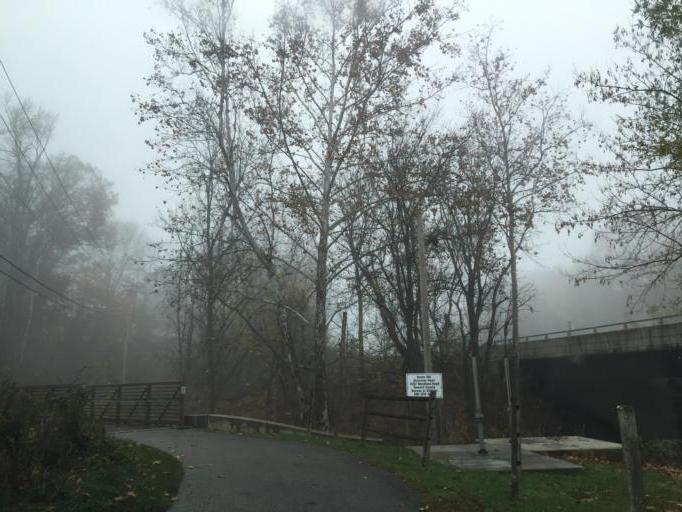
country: US
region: Maryland
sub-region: Howard County
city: Columbia
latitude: 39.2398
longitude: -76.8474
